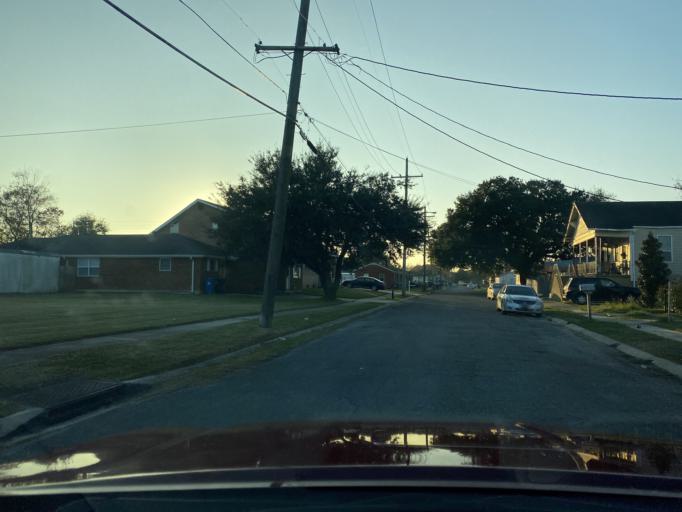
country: US
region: Louisiana
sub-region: Orleans Parish
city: New Orleans
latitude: 30.0197
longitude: -90.0474
